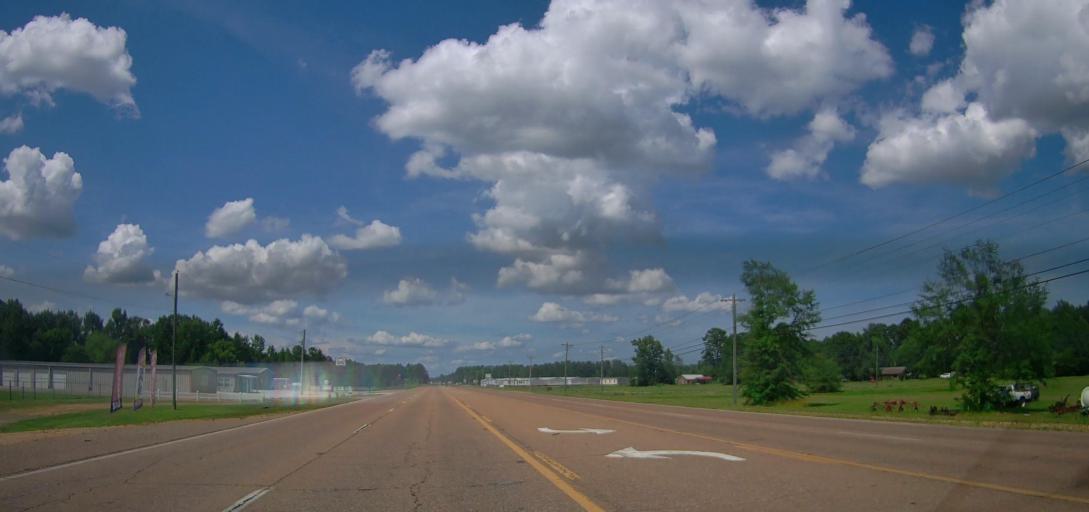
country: US
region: Mississippi
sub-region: Lowndes County
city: Columbus Air Force Base
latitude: 33.5917
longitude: -88.4258
